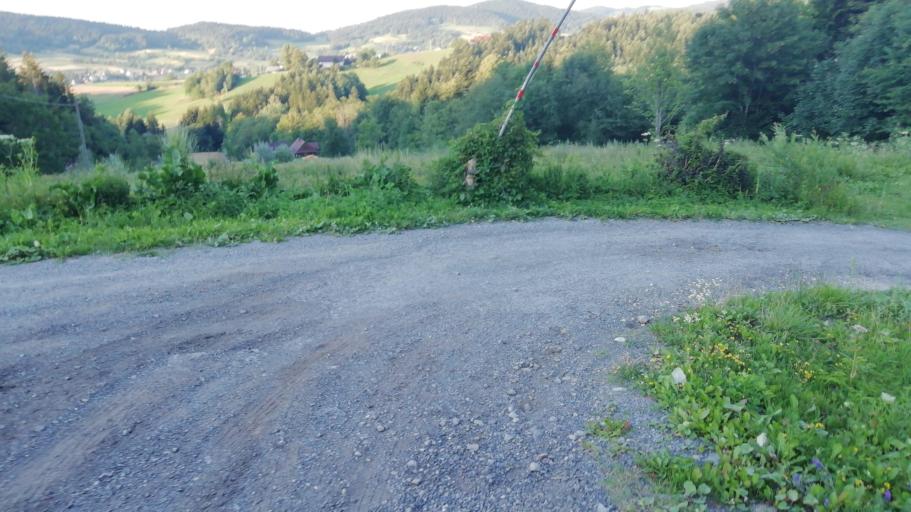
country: PL
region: Lesser Poland Voivodeship
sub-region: Powiat limanowski
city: Kasina Wielka
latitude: 49.7194
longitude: 20.1126
